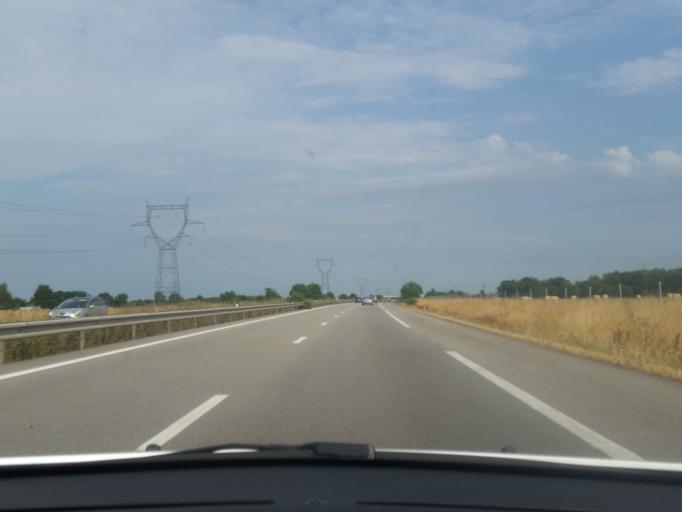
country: FR
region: Pays de la Loire
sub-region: Departement de la Loire-Atlantique
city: Varades
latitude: 47.4219
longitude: -1.0399
